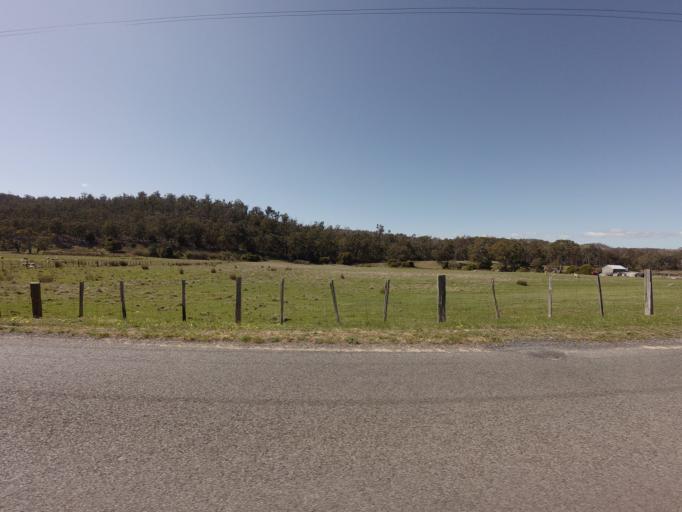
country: AU
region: Tasmania
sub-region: Derwent Valley
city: New Norfolk
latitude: -42.6663
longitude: 146.7880
